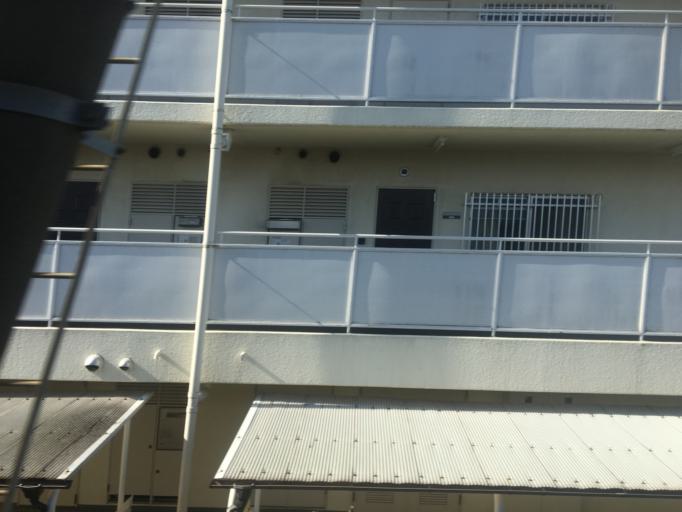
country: JP
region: Saitama
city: Kawagoe
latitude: 35.9187
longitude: 139.4718
